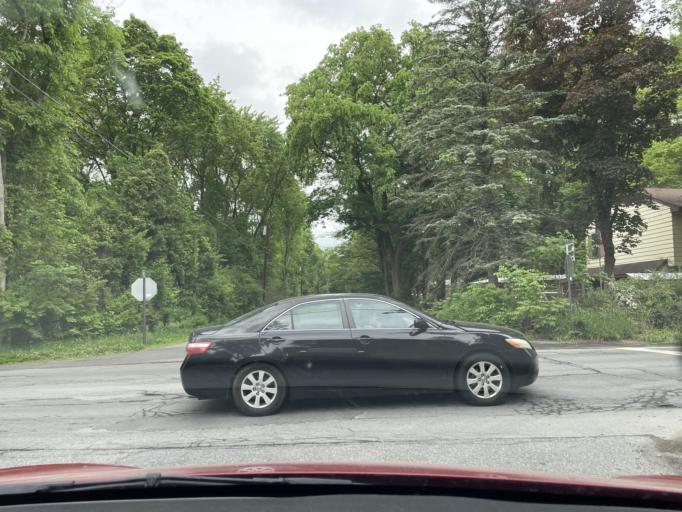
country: US
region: New York
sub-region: Ulster County
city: New Paltz
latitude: 41.7501
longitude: -74.0771
